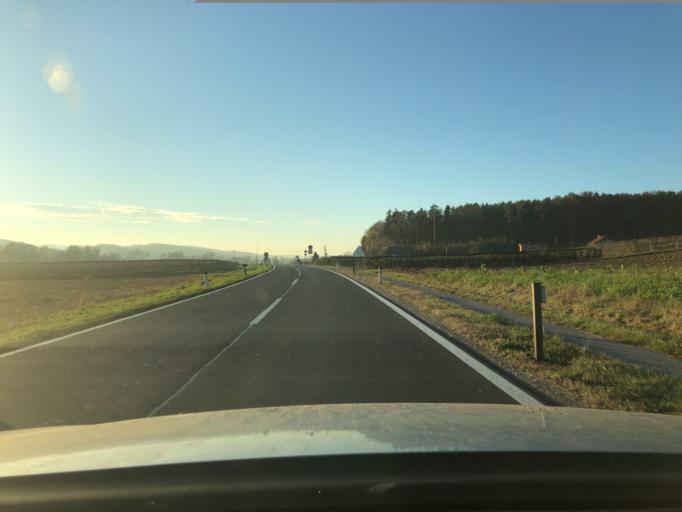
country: AT
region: Styria
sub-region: Politischer Bezirk Hartberg-Fuerstenfeld
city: Nestelbach im Ilztal
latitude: 47.0940
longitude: 15.8688
